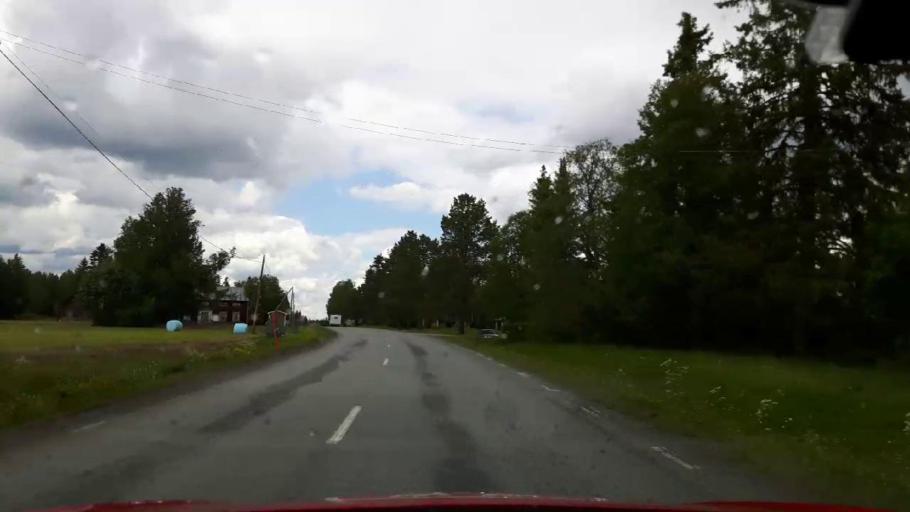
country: SE
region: Jaemtland
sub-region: Krokoms Kommun
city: Krokom
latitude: 63.5163
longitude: 14.2307
